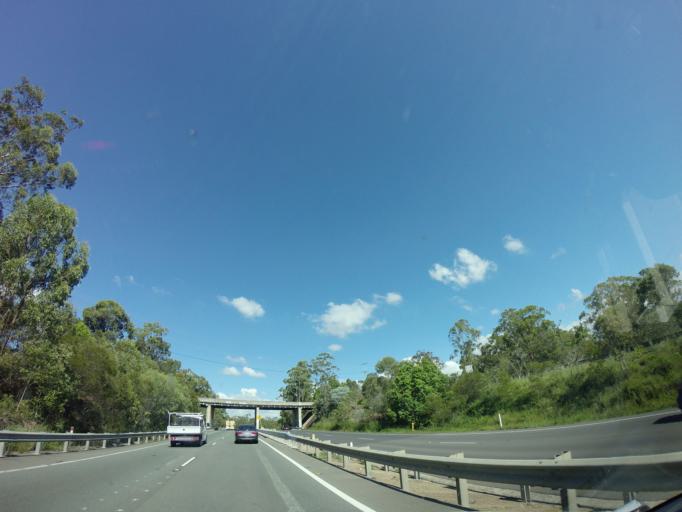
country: AU
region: Queensland
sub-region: Ipswich
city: Brassall
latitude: -27.5806
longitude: 152.7524
